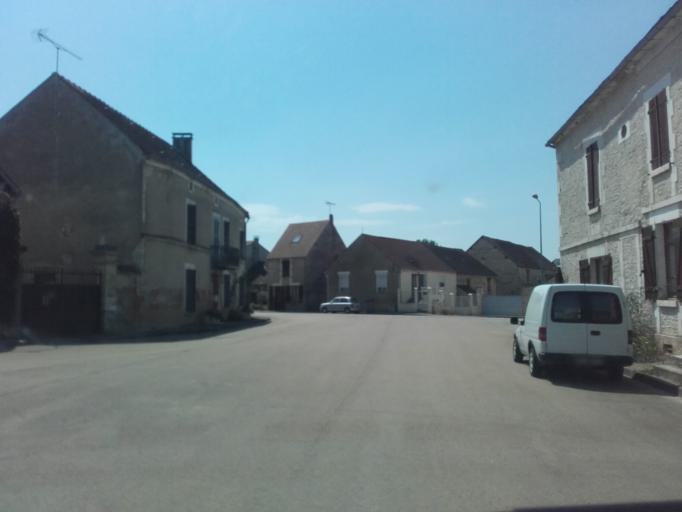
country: FR
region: Bourgogne
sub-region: Departement de l'Yonne
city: Chablis
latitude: 47.7279
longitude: 3.8539
